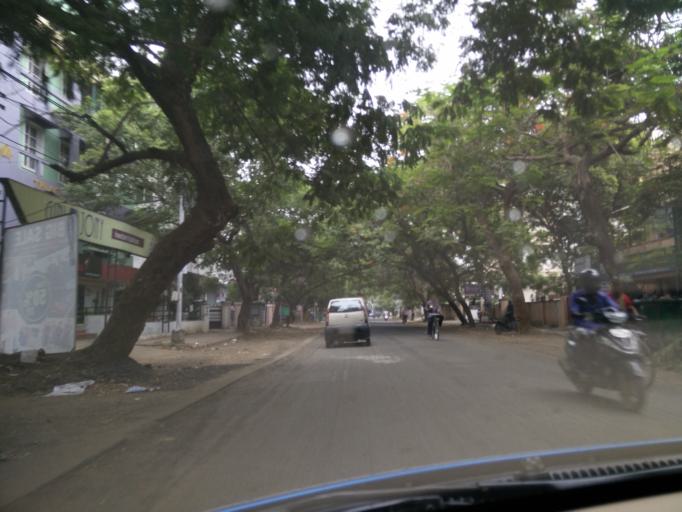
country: IN
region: Tamil Nadu
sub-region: Chennai
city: Gandhi Nagar
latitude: 12.9972
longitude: 80.2517
